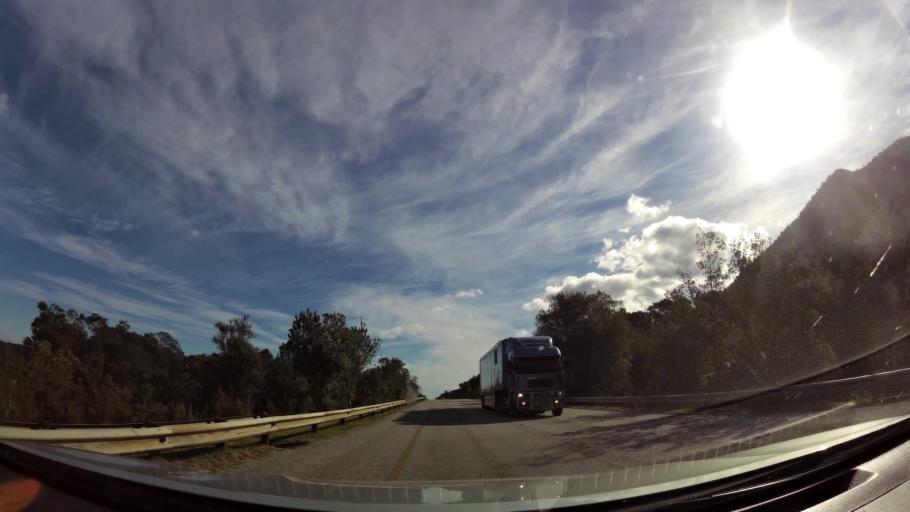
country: ZA
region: Eastern Cape
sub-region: Cacadu District Municipality
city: Kareedouw
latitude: -33.9919
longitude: 24.1561
